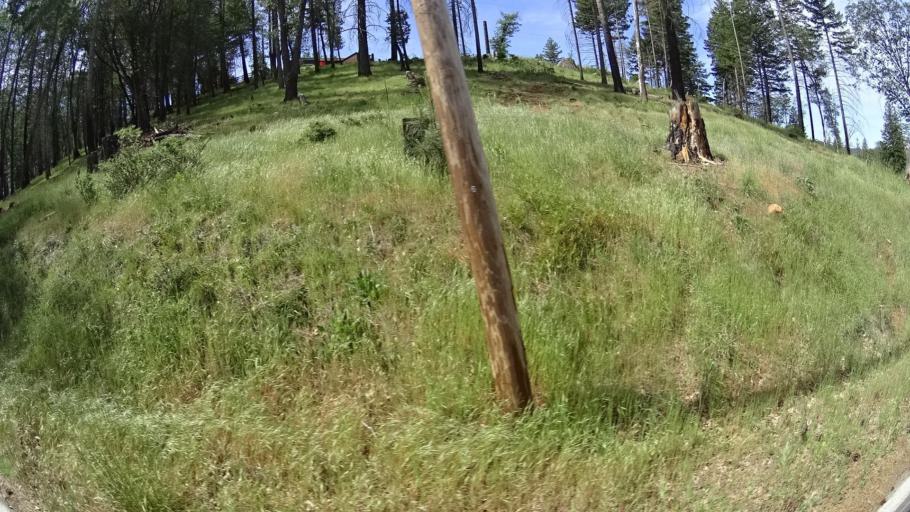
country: US
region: California
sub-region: Lake County
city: Cobb
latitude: 38.8467
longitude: -122.7278
